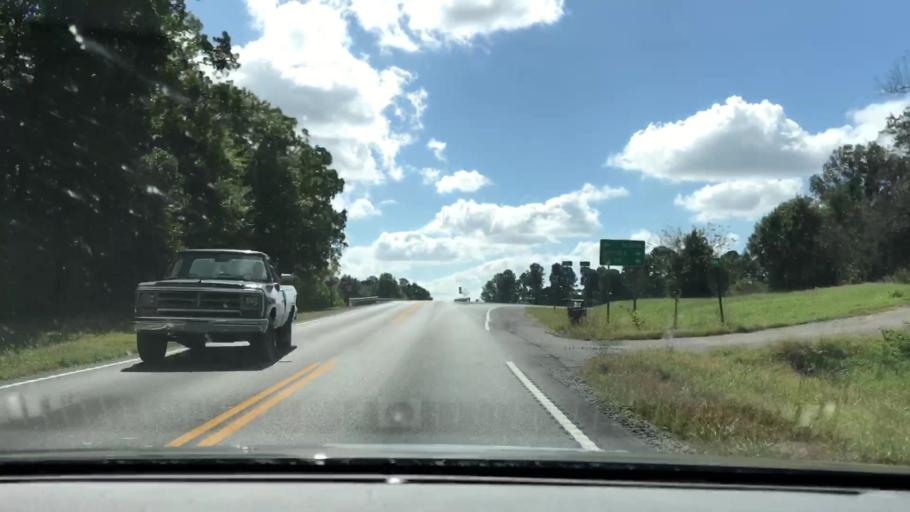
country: US
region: Kentucky
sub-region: Graves County
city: Mayfield
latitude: 36.7777
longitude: -88.5959
